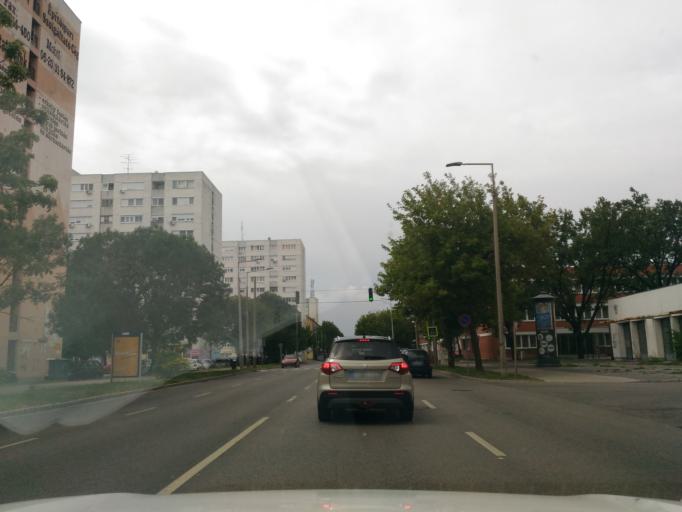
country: HU
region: Jasz-Nagykun-Szolnok
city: Szolnok
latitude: 47.1767
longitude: 20.1991
